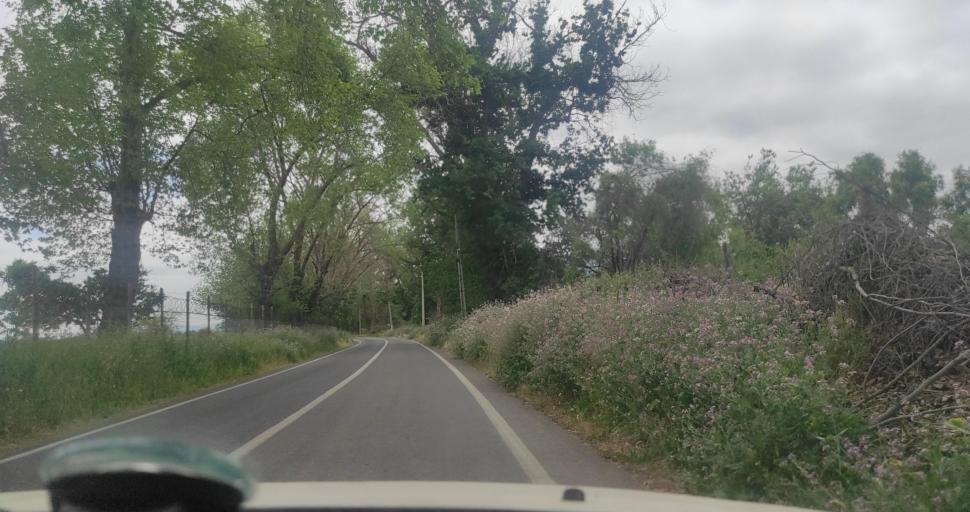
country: CL
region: Valparaiso
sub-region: Provincia de Marga Marga
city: Limache
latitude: -33.0268
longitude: -71.2394
